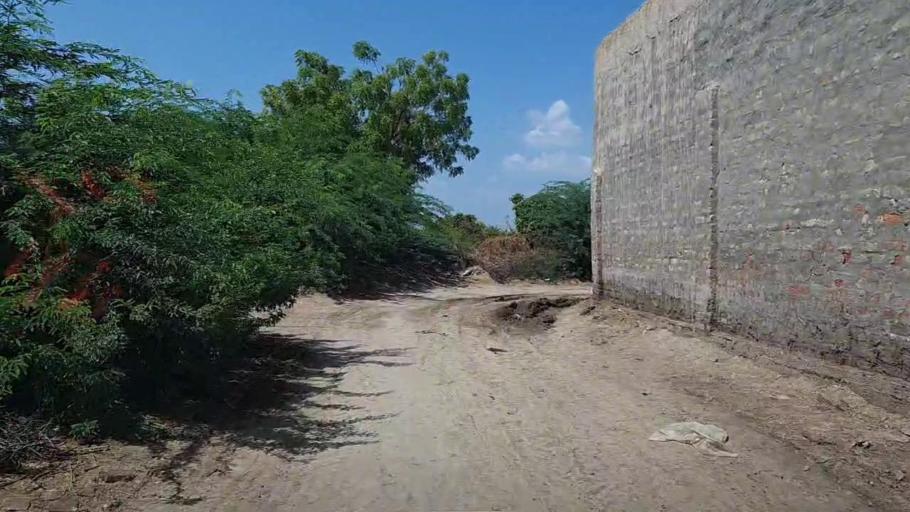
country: PK
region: Sindh
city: Bhiria
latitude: 26.9517
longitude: 68.2318
